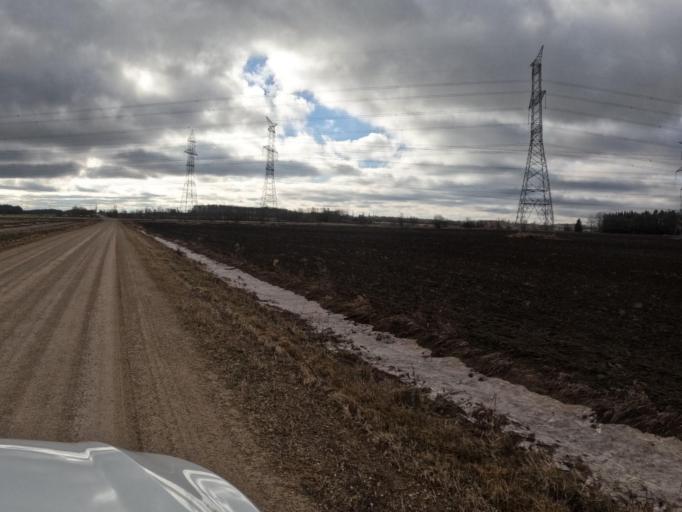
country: CA
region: Ontario
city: Shelburne
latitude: 43.9890
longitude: -80.3846
